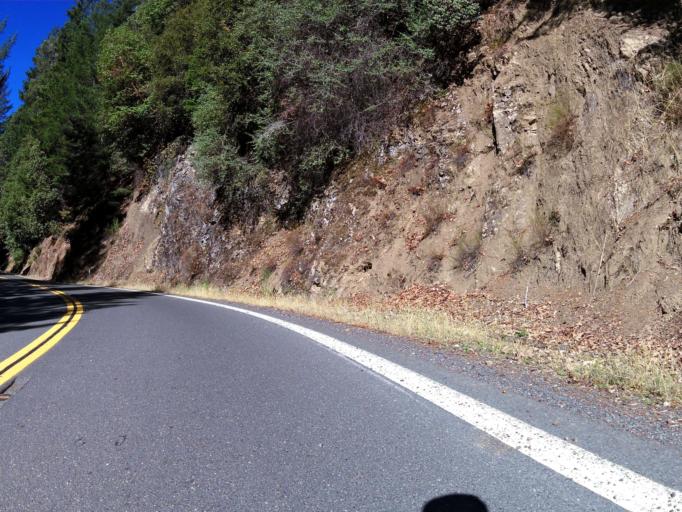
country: US
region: California
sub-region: Humboldt County
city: Redway
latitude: 39.8493
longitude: -123.7400
